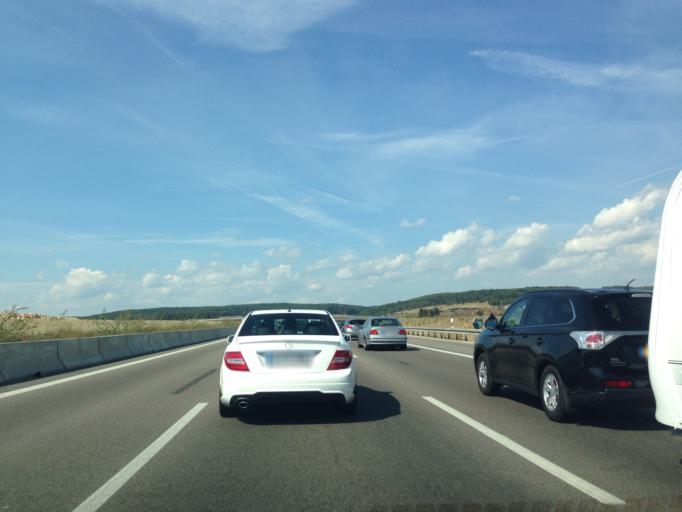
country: DE
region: Baden-Wuerttemberg
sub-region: Tuebingen Region
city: Dornstadt
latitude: 48.4805
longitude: 9.8724
